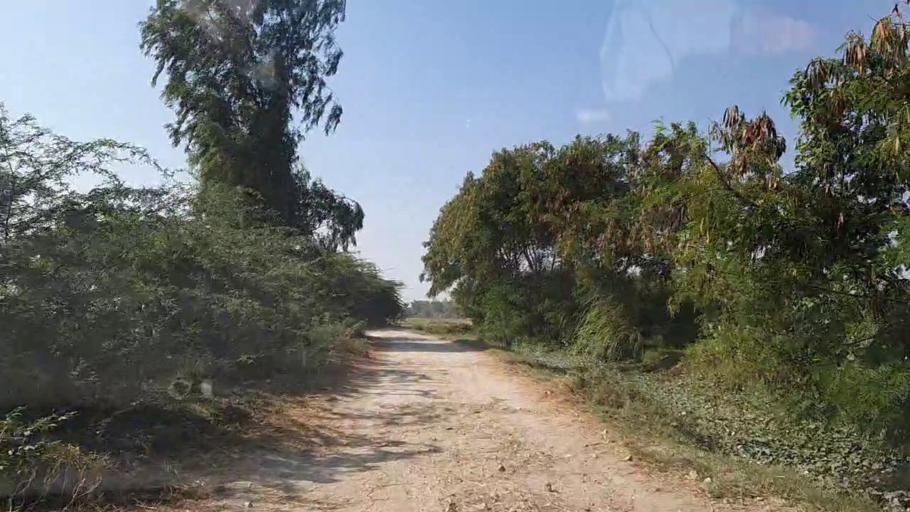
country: PK
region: Sindh
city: Thatta
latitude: 24.7873
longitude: 67.9476
